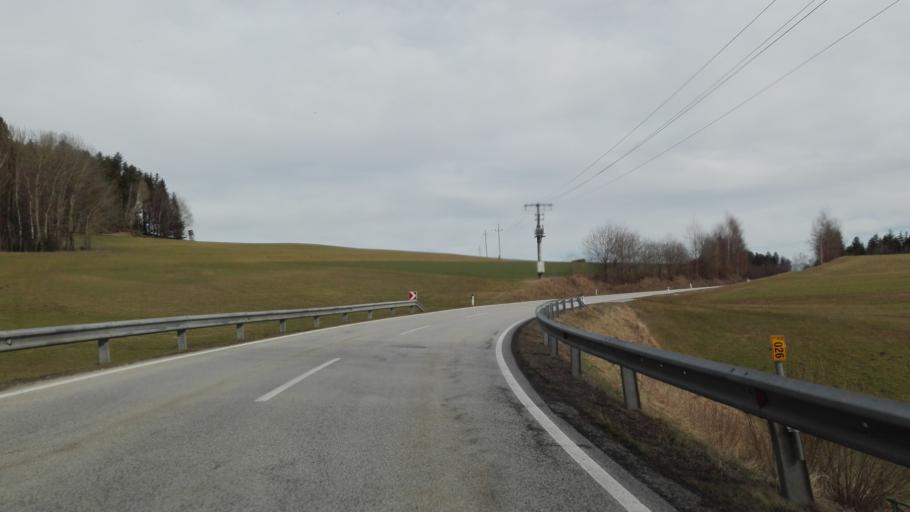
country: AT
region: Upper Austria
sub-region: Politischer Bezirk Rohrbach
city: Schlaegl
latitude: 48.6067
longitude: 13.9253
